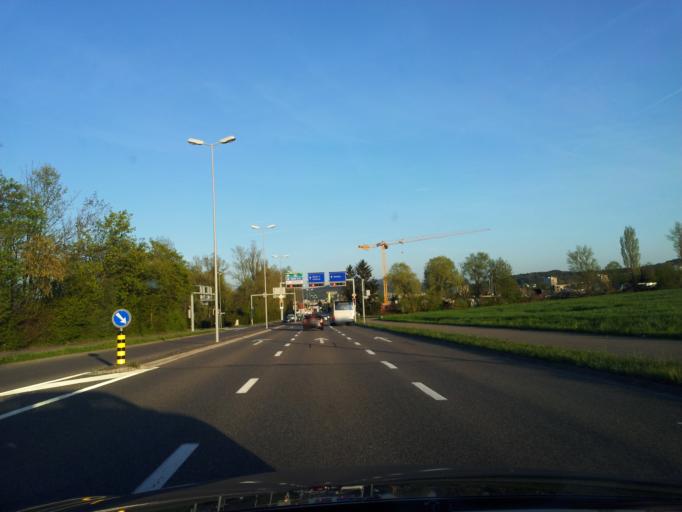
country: CH
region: Zurich
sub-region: Bezirk Dietikon
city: Dietikon / Almend
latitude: 47.4131
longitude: 8.3821
